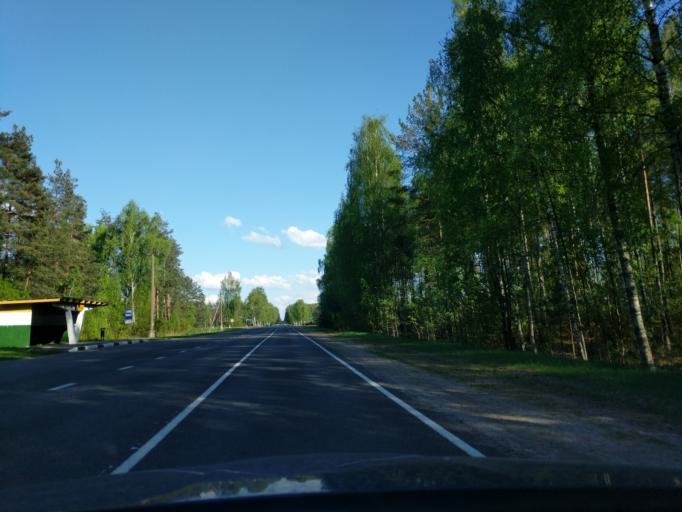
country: BY
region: Minsk
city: Myadzyel
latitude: 54.8161
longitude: 26.9682
